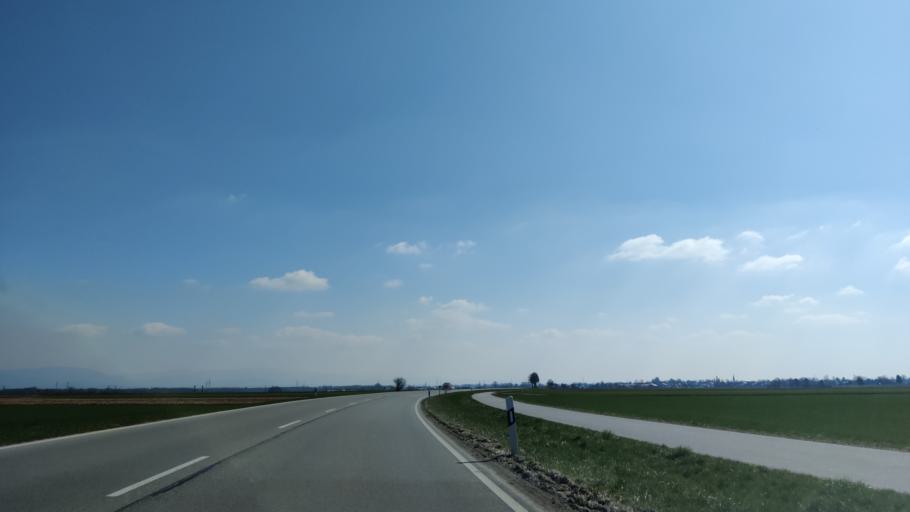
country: DE
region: Bavaria
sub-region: Lower Bavaria
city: Strasskirchen
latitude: 48.8391
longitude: 12.6895
